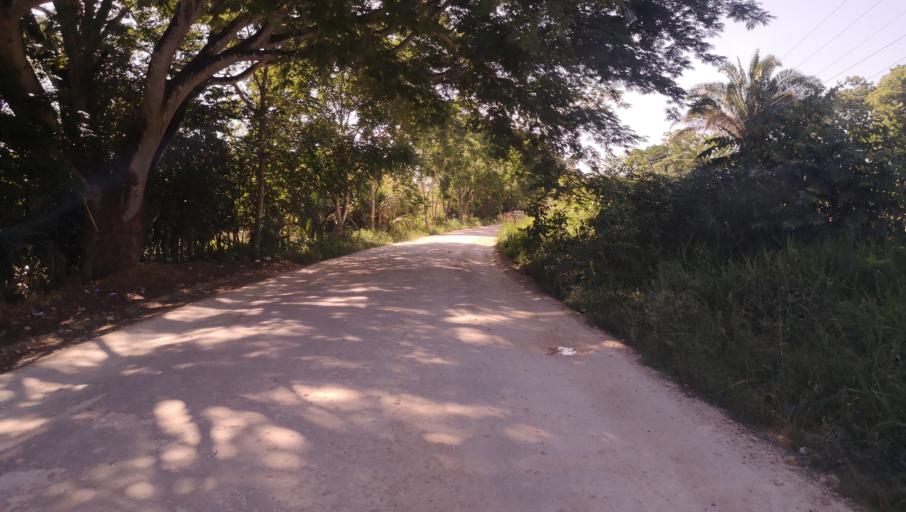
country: GT
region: Peten
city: Dolores
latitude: 16.7207
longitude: -89.3743
